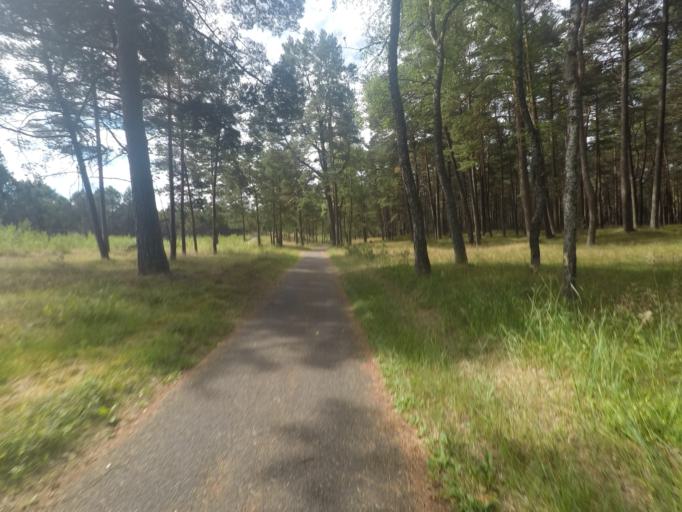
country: LT
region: Klaipedos apskritis
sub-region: Klaipeda
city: Klaipeda
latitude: 55.6139
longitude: 21.1217
